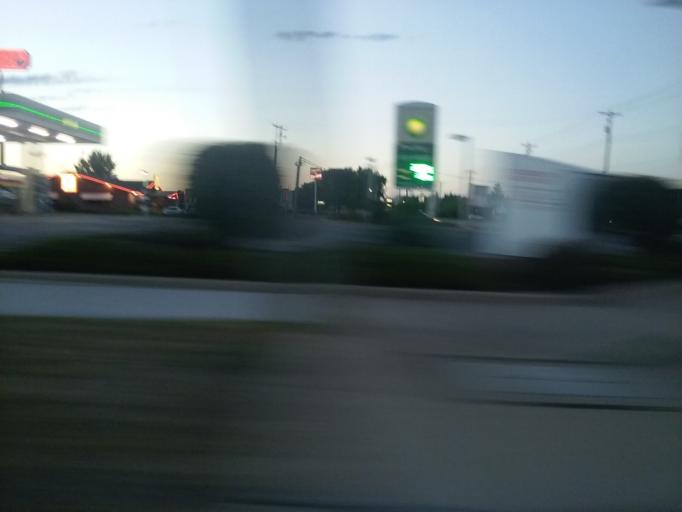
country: US
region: Ohio
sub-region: Hancock County
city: Findlay
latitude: 41.0588
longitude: -83.6647
